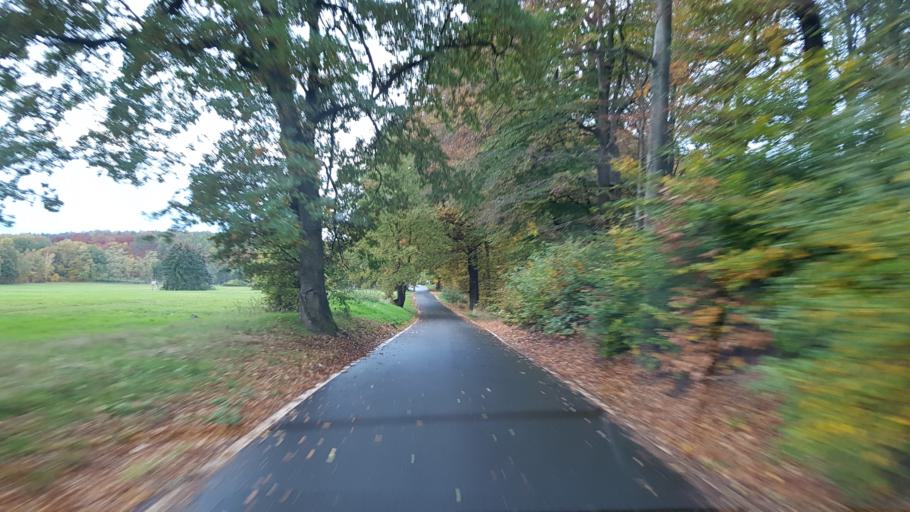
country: DE
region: Saxony
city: Cavertitz
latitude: 51.4161
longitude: 13.0736
